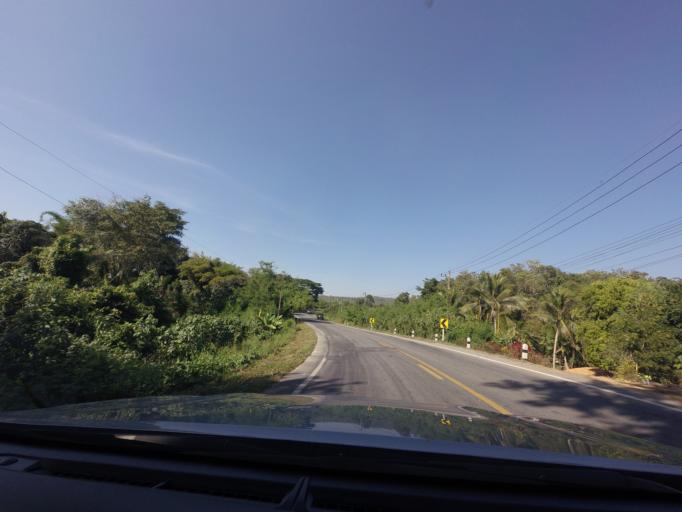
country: TH
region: Sukhothai
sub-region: Amphoe Si Satchanalai
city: Si Satchanalai
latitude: 17.6254
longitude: 99.7017
